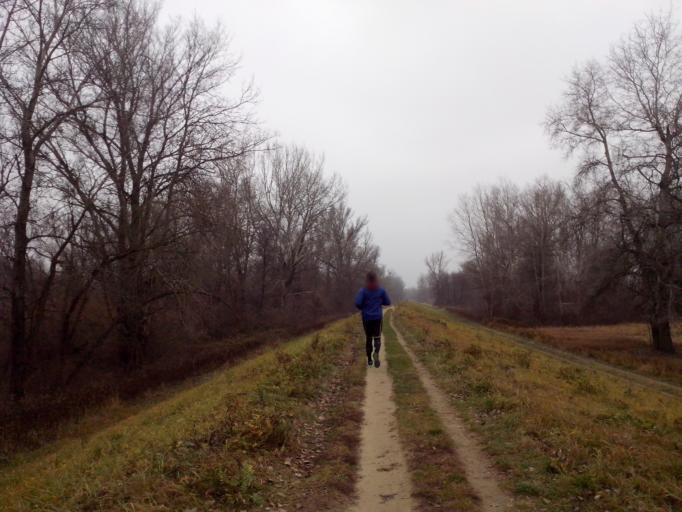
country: PL
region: Masovian Voivodeship
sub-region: Powiat legionowski
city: Jablonna
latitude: 52.3544
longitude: 20.9207
